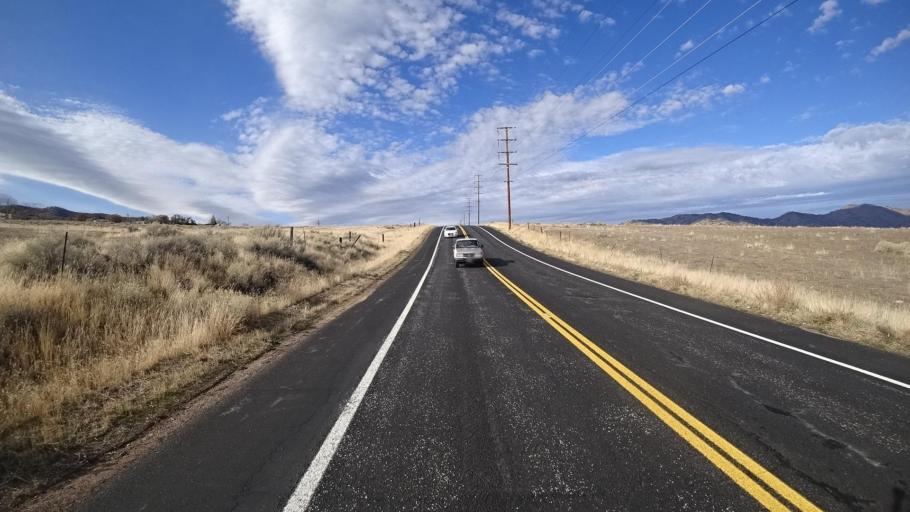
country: US
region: California
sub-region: Kern County
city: Golden Hills
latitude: 35.1082
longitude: -118.4861
